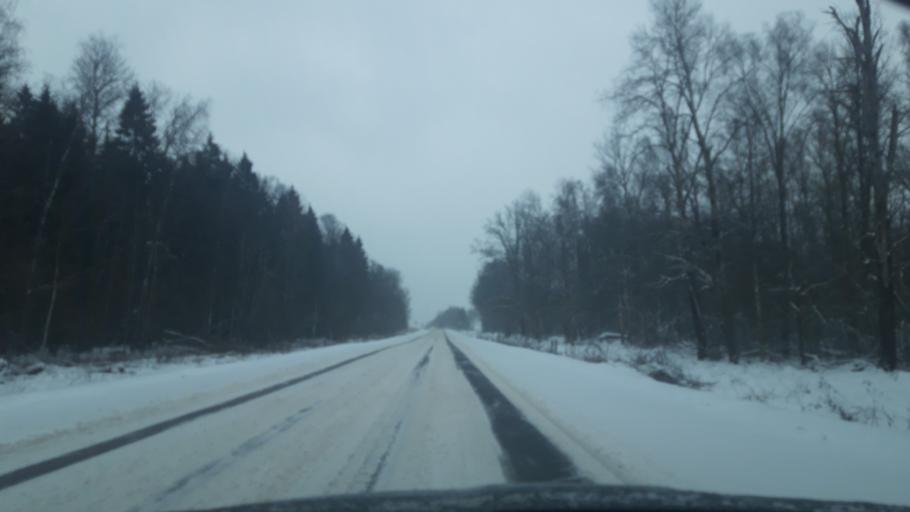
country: RU
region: Moskovskaya
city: Yakhroma
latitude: 56.2955
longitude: 37.4039
